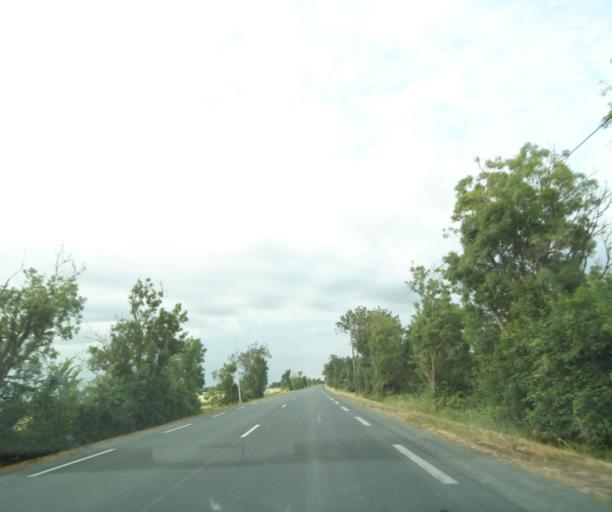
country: FR
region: Poitou-Charentes
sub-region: Departement de la Charente-Maritime
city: Marans
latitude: 46.3563
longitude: -0.9926
